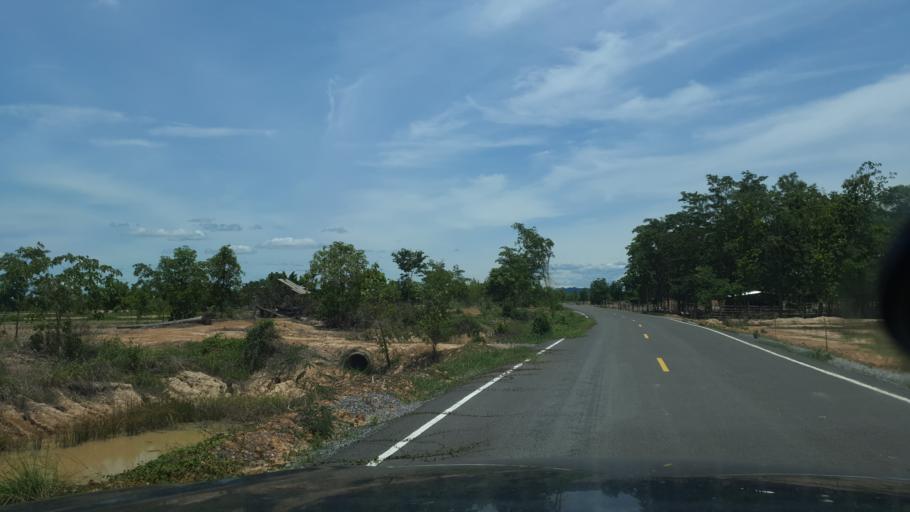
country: TH
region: Sukhothai
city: Ban Na
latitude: 17.1508
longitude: 99.6541
